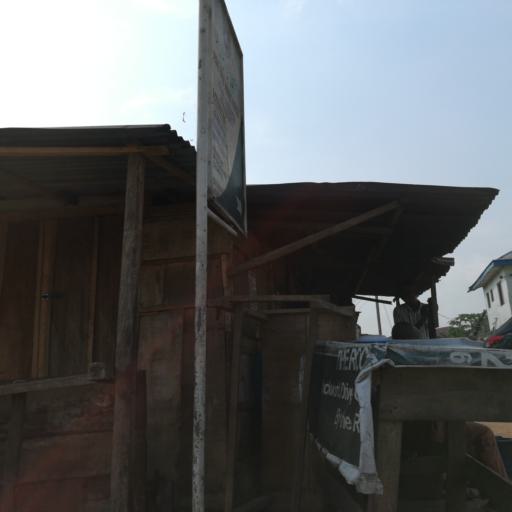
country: NG
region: Rivers
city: Port Harcourt
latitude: 4.8413
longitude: 7.0648
